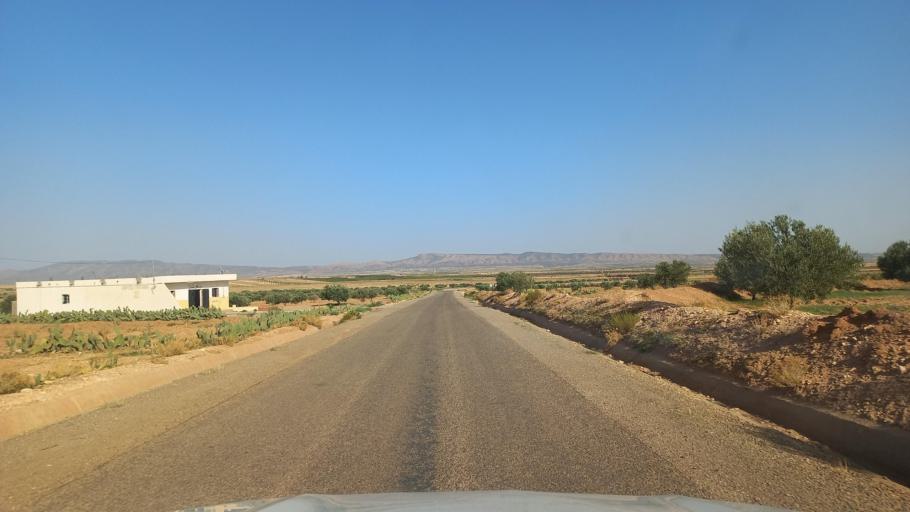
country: TN
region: Al Qasrayn
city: Sbiba
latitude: 35.3785
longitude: 9.0269
